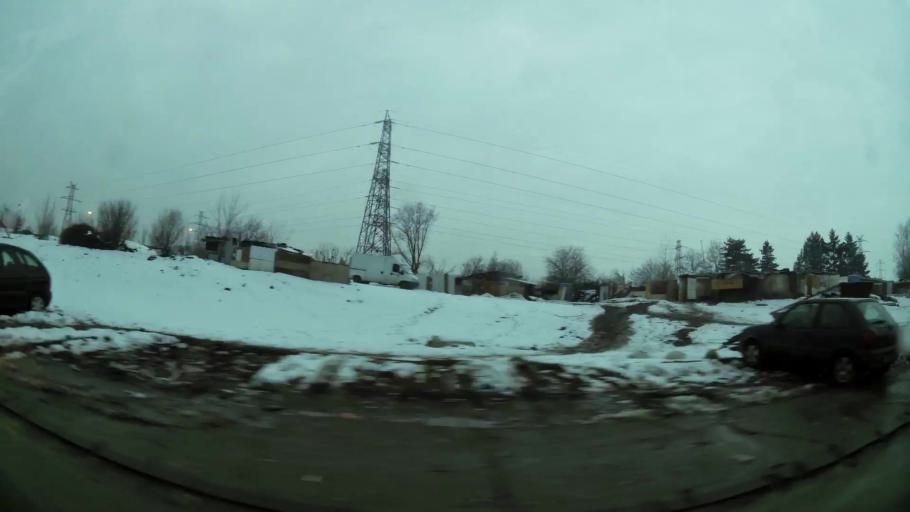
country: RS
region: Central Serbia
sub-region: Belgrade
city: Zemun
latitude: 44.8082
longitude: 20.3628
